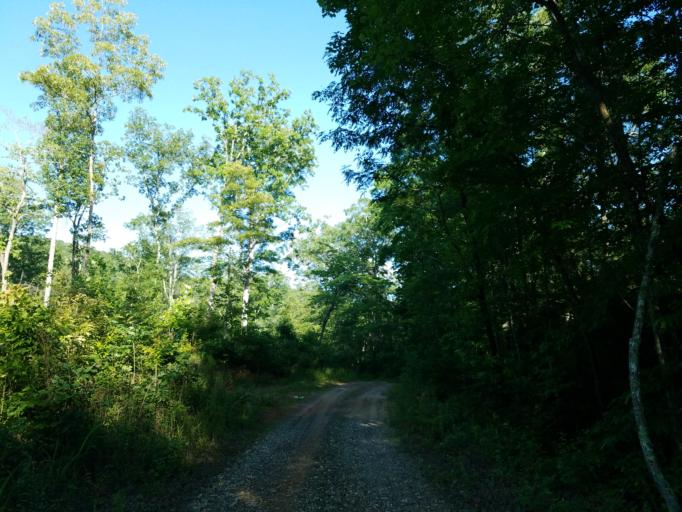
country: US
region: Georgia
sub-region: Fannin County
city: Blue Ridge
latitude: 34.7982
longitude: -84.1868
